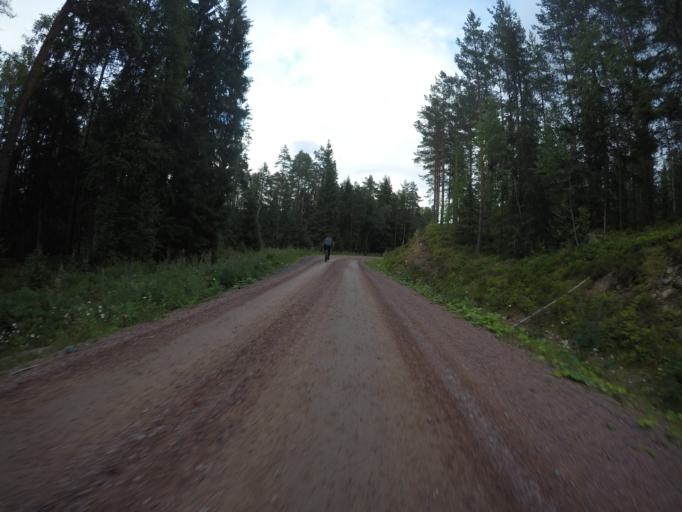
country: SE
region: OErebro
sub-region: Hallefors Kommun
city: Haellefors
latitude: 60.0389
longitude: 14.4911
